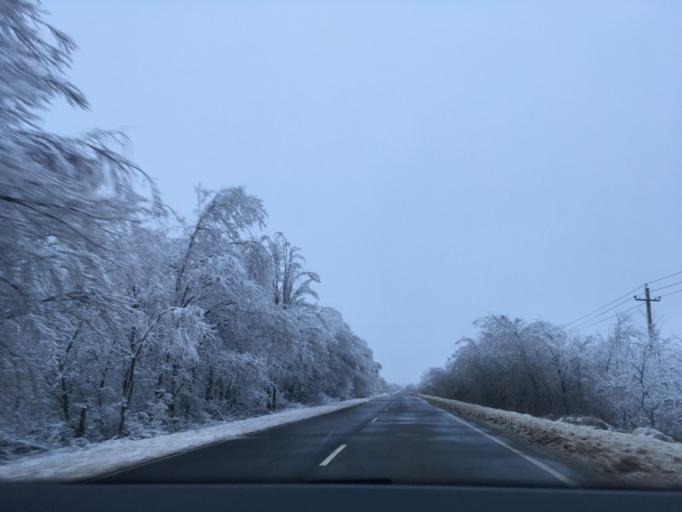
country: RU
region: Voronezj
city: Verkhniy Mamon
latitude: 50.0228
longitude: 40.0857
